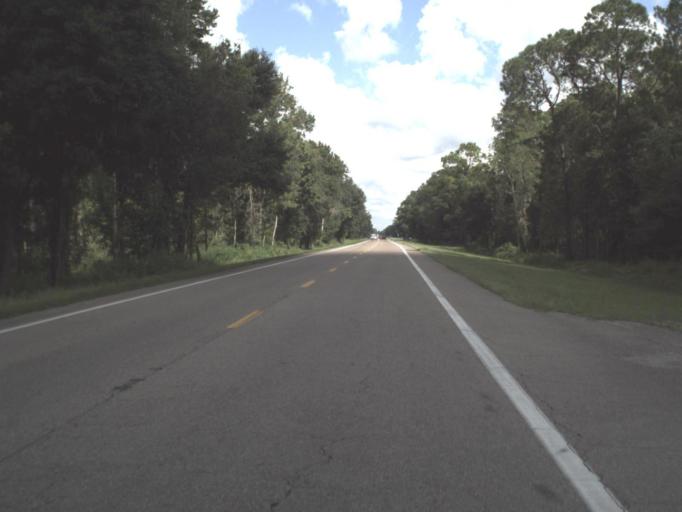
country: US
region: Florida
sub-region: Polk County
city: Polk City
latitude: 28.2135
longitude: -81.8204
